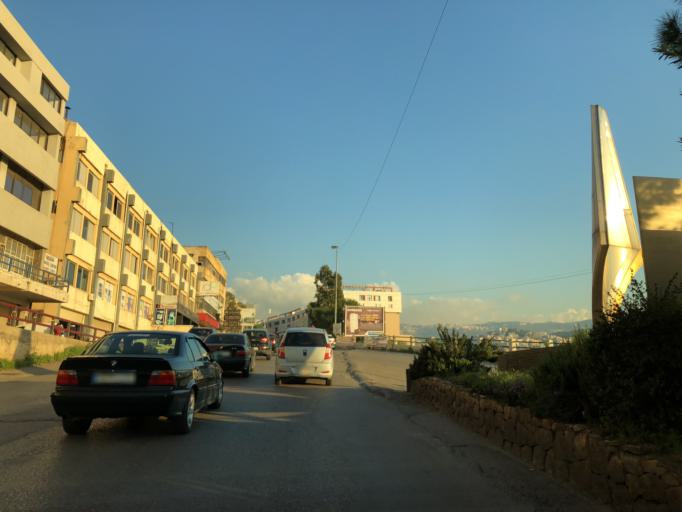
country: LB
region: Mont-Liban
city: Baabda
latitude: 33.8618
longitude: 35.5500
